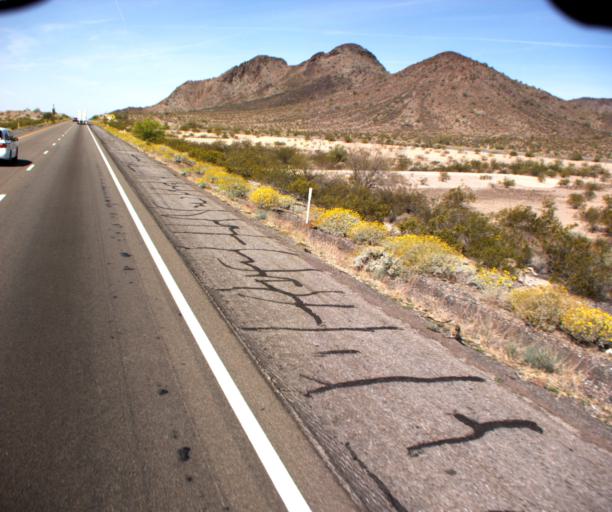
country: US
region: Arizona
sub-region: La Paz County
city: Salome
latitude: 33.6096
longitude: -113.6215
